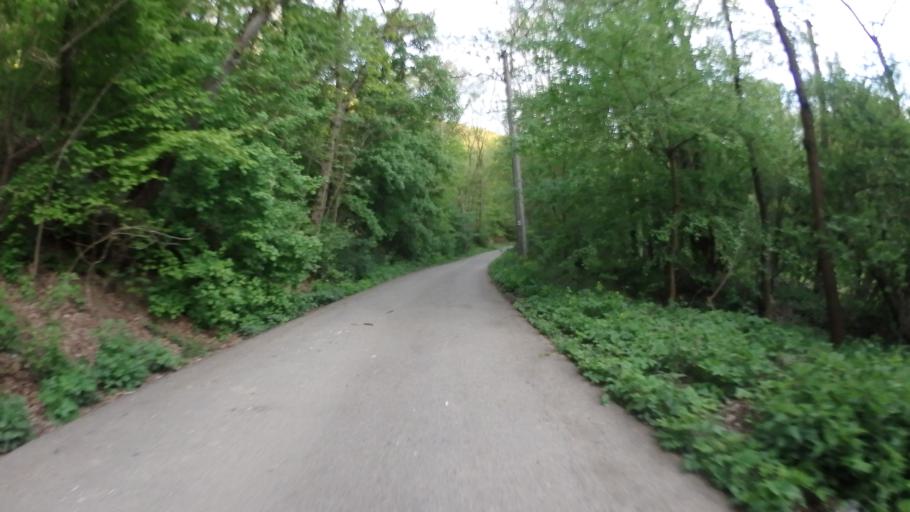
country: CZ
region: South Moravian
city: Strelice
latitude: 49.1407
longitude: 16.4774
